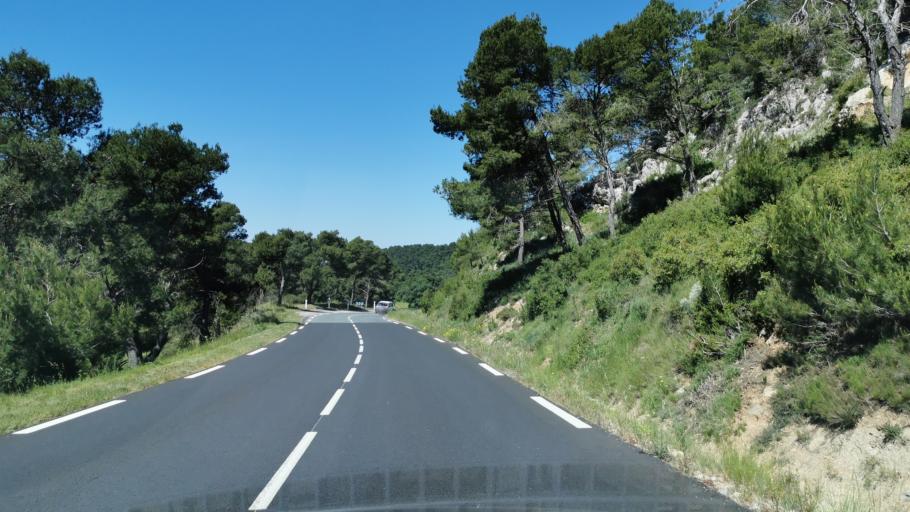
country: FR
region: Languedoc-Roussillon
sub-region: Departement de l'Aude
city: Armissan
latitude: 43.1746
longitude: 3.0865
